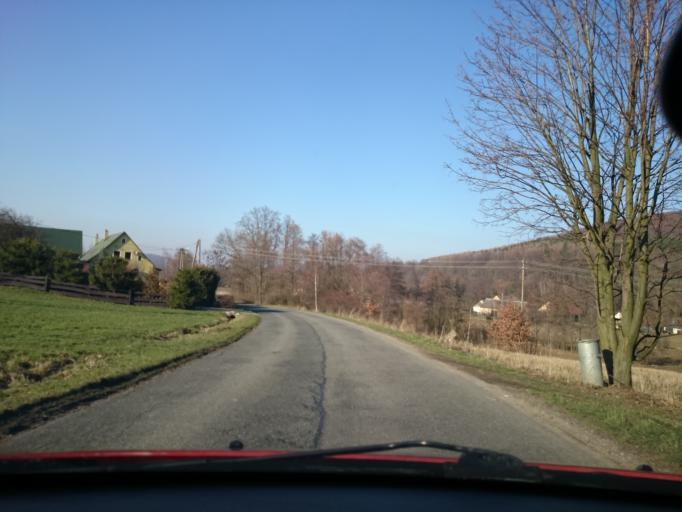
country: PL
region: Lower Silesian Voivodeship
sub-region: Powiat klodzki
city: Bystrzyca Klodzka
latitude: 50.3636
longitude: 16.6377
